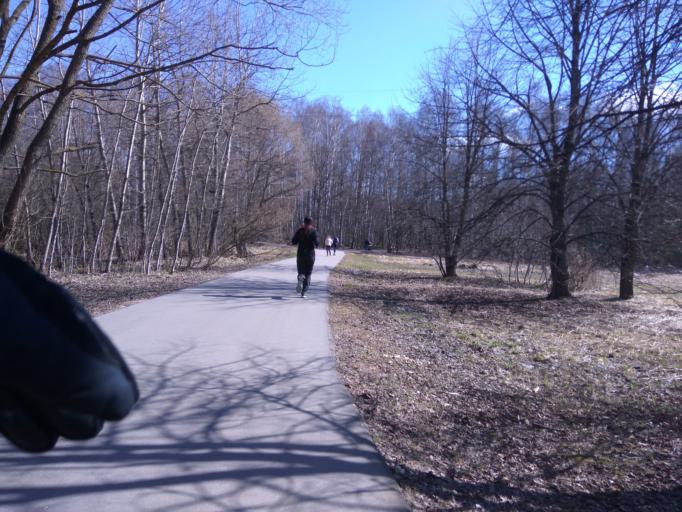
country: RU
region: Moscow
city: Ivanovskoye
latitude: 55.7865
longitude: 37.8309
